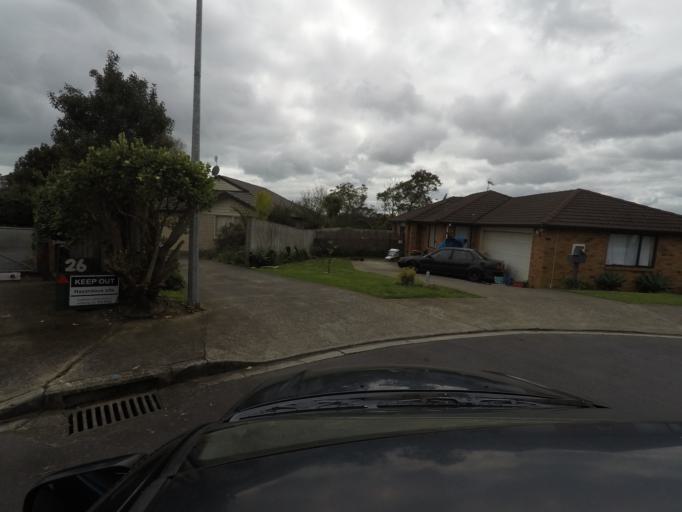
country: NZ
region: Auckland
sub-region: Auckland
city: Tamaki
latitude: -36.9322
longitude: 174.8548
